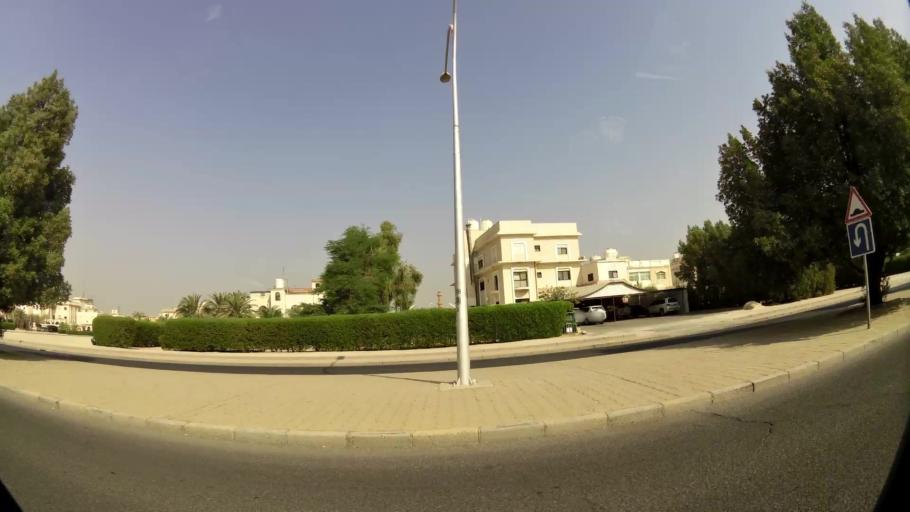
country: KW
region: Al Asimah
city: Ar Rabiyah
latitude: 29.2883
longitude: 47.9004
